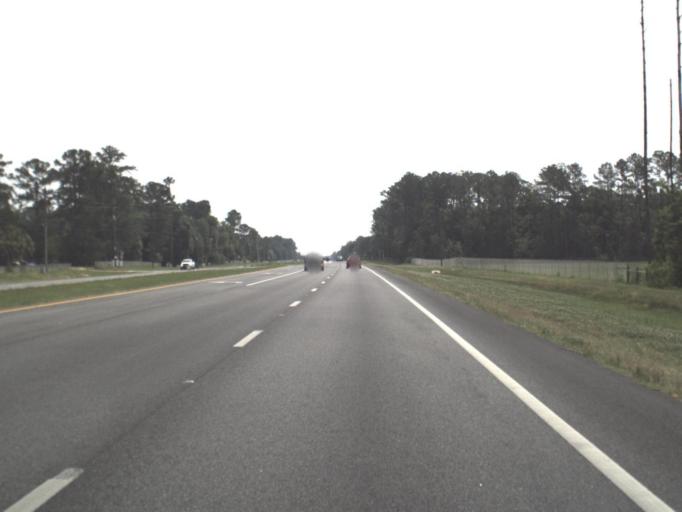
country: US
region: Florida
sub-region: Nassau County
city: Callahan
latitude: 30.5890
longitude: -81.7903
